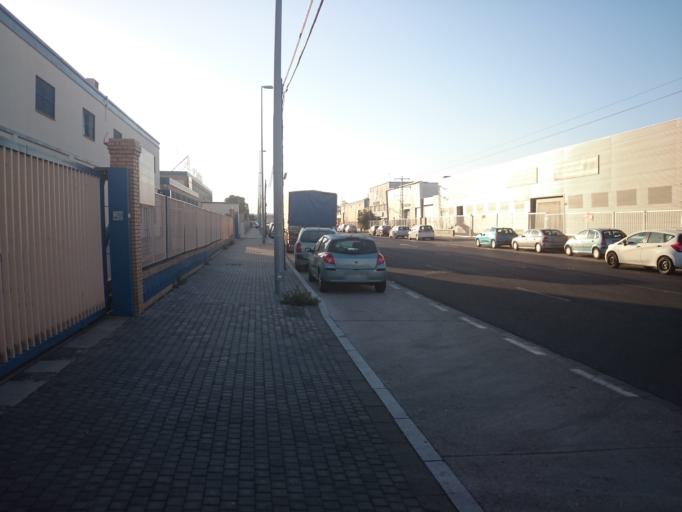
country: ES
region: Andalusia
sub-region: Provincia de Sevilla
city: Sevilla
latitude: 37.3900
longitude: -5.9569
